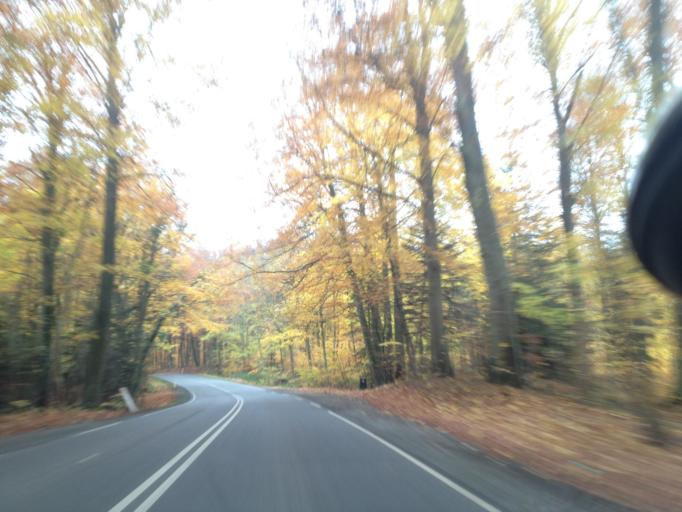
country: DK
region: South Denmark
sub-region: Assens Kommune
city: Vissenbjerg
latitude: 55.4452
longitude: 10.1686
